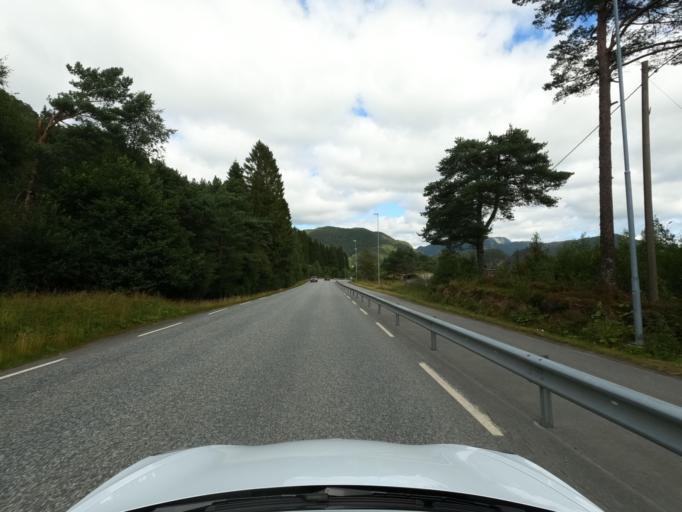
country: NO
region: Hordaland
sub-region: Os
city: Hagavik
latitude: 60.1917
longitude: 5.4194
